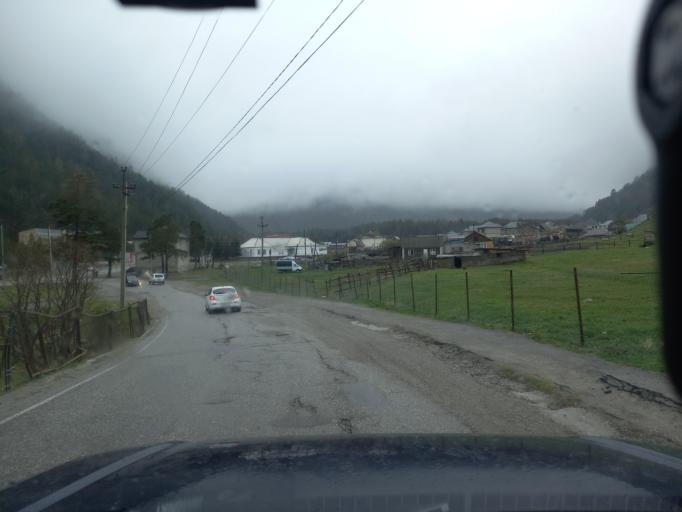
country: RU
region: Kabardino-Balkariya
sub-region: El'brusskiy Rayon
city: El'brus
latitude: 43.2563
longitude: 42.6468
